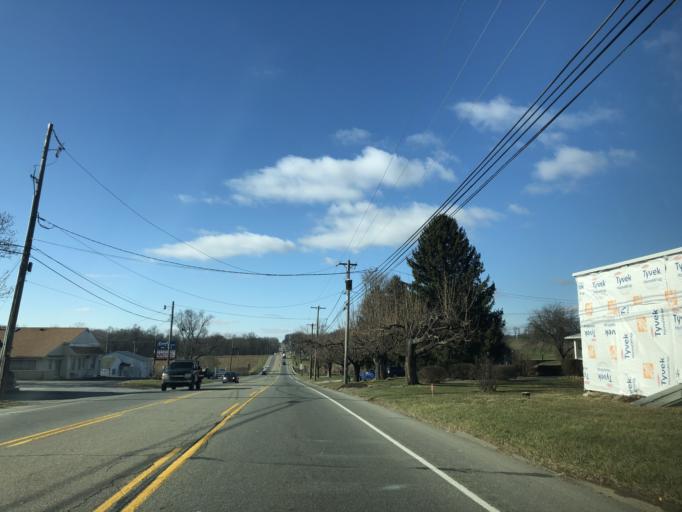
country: US
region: Pennsylvania
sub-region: Chester County
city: Atglen
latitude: 39.9856
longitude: -75.9528
